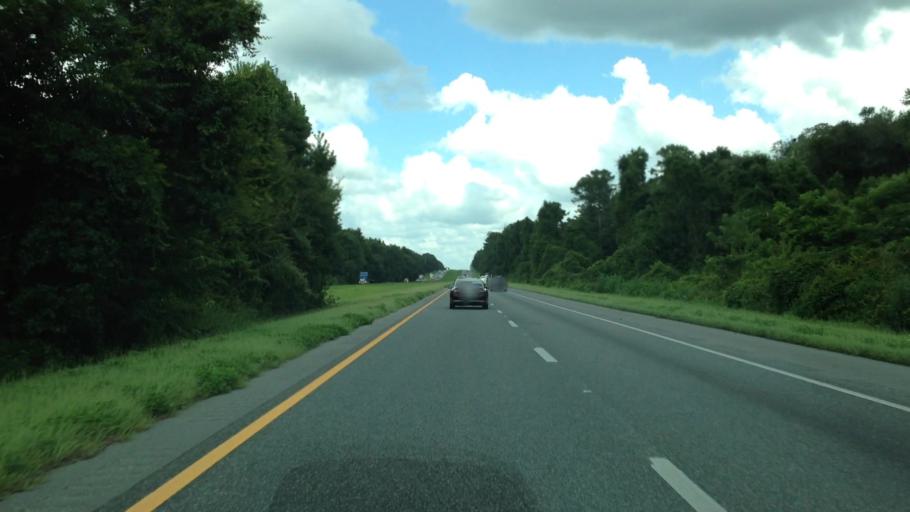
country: US
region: Florida
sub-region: Madison County
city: Madison
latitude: 30.4308
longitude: -83.5547
